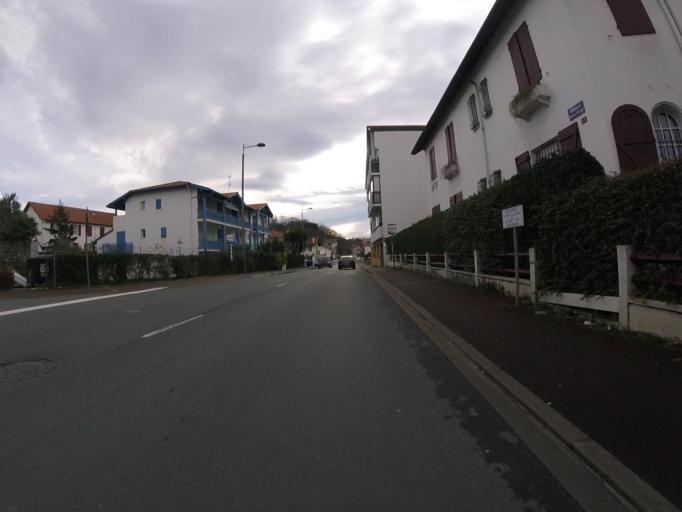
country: FR
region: Aquitaine
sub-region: Departement des Pyrenees-Atlantiques
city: Hendaye
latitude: 43.3704
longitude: -1.7723
